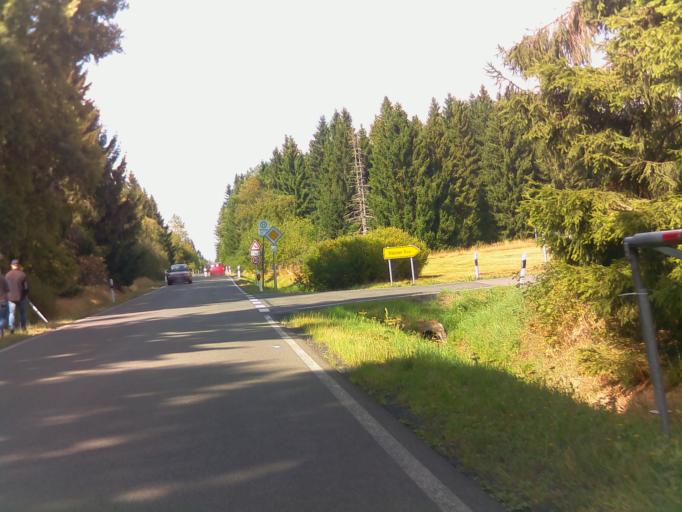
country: DE
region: Thuringia
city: Birx
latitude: 50.5125
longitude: 10.0735
